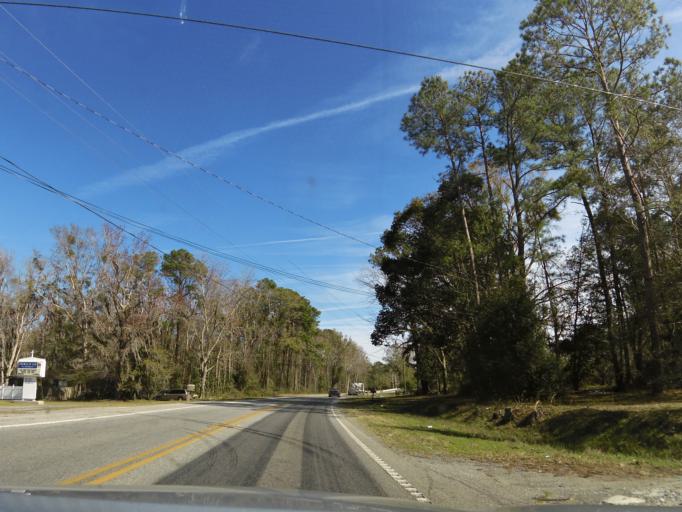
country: US
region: Georgia
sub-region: Glynn County
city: Dock Junction
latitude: 31.2742
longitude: -81.5773
